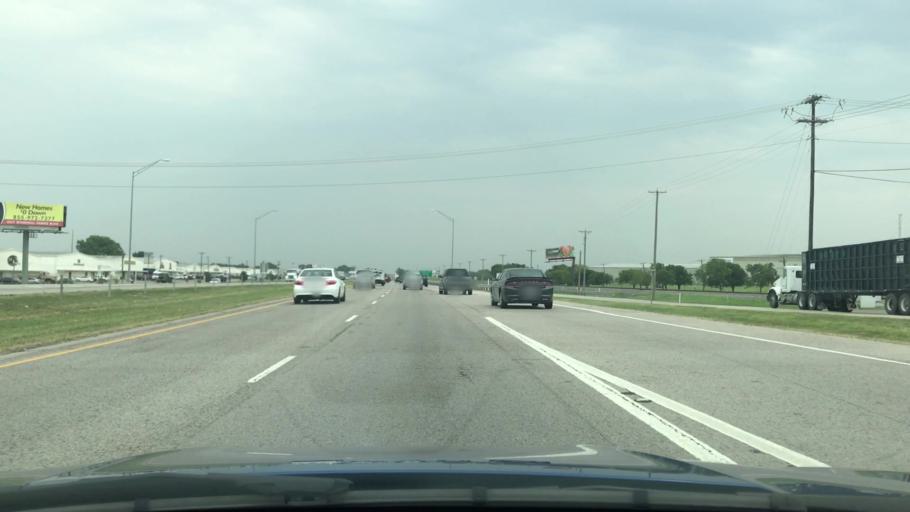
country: US
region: Texas
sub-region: Kaufman County
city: Forney
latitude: 32.7413
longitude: -96.4422
